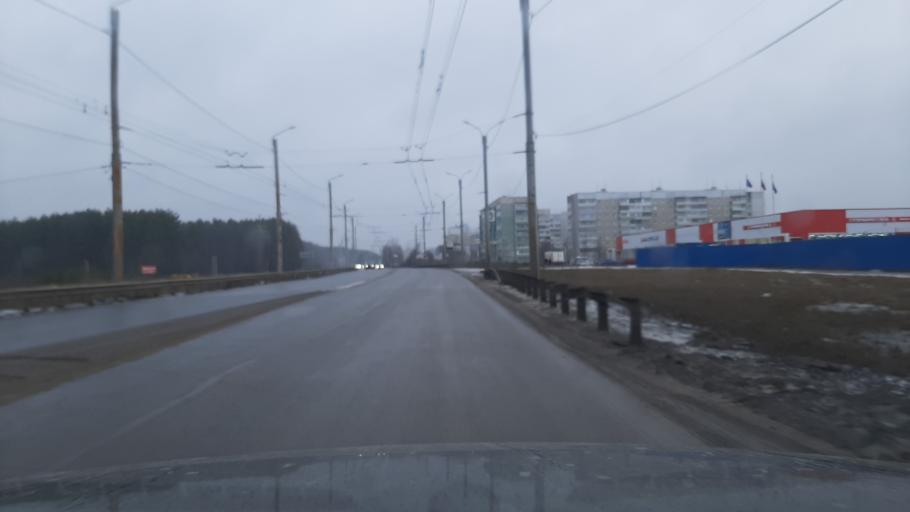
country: RU
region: Ivanovo
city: Kokhma
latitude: 56.9463
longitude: 41.0553
